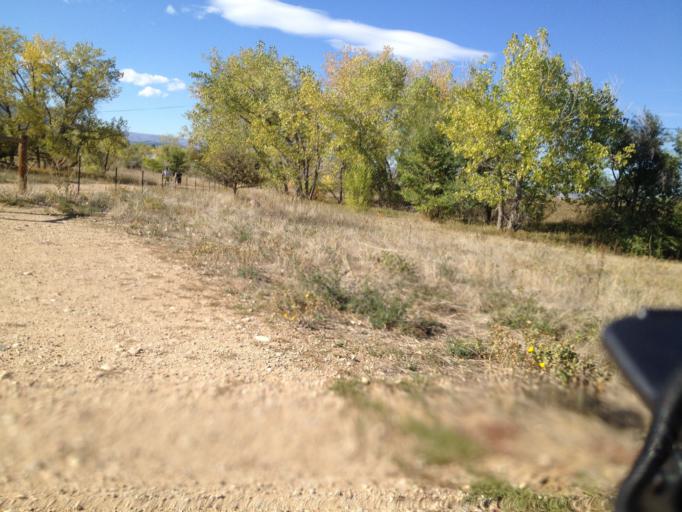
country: US
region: Colorado
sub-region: Boulder County
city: Boulder
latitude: 39.9821
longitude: -105.2330
